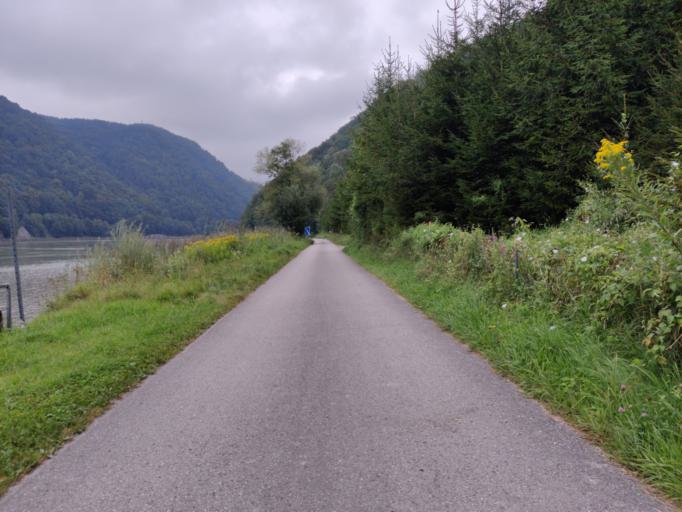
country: AT
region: Lower Austria
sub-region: Politischer Bezirk Melk
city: Nochling
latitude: 48.2303
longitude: 14.9075
